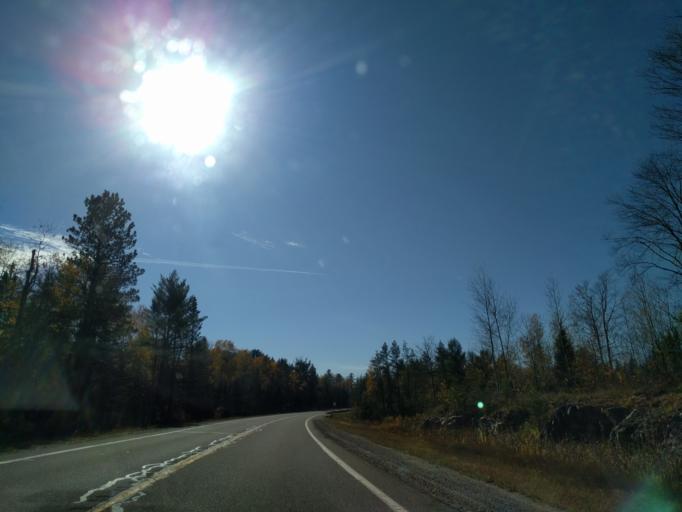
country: US
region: Michigan
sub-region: Marquette County
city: West Ishpeming
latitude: 46.4613
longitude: -87.9352
